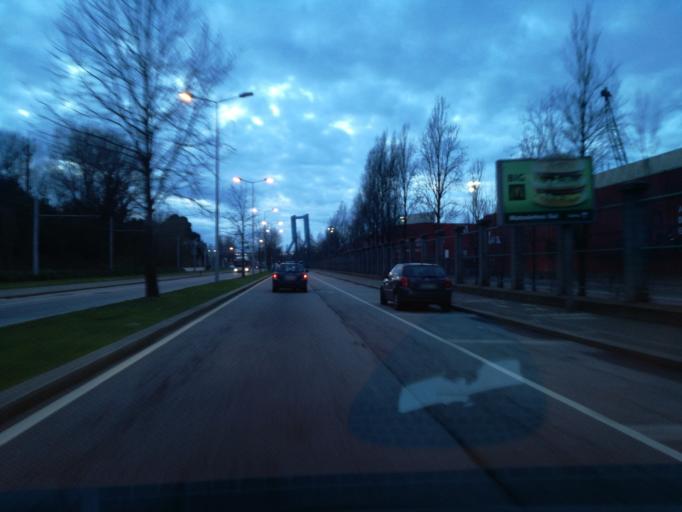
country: PT
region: Porto
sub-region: Matosinhos
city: Matosinhos
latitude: 41.1884
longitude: -8.6887
